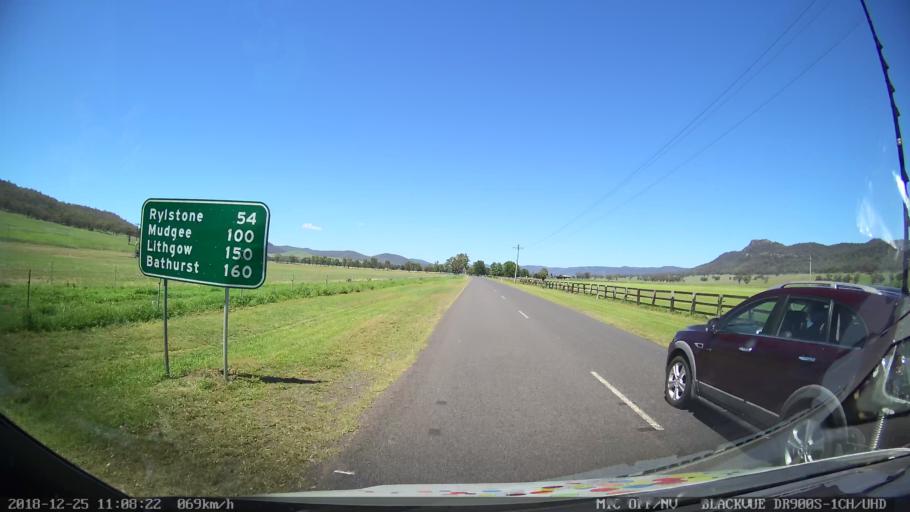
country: AU
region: New South Wales
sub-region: Upper Hunter Shire
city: Merriwa
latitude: -32.4015
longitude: 150.1253
